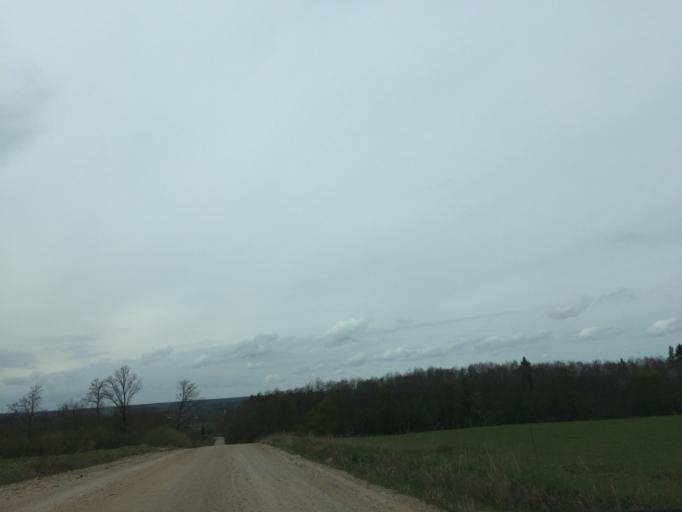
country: LV
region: Priekuli
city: Priekuli
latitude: 57.3428
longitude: 25.3514
